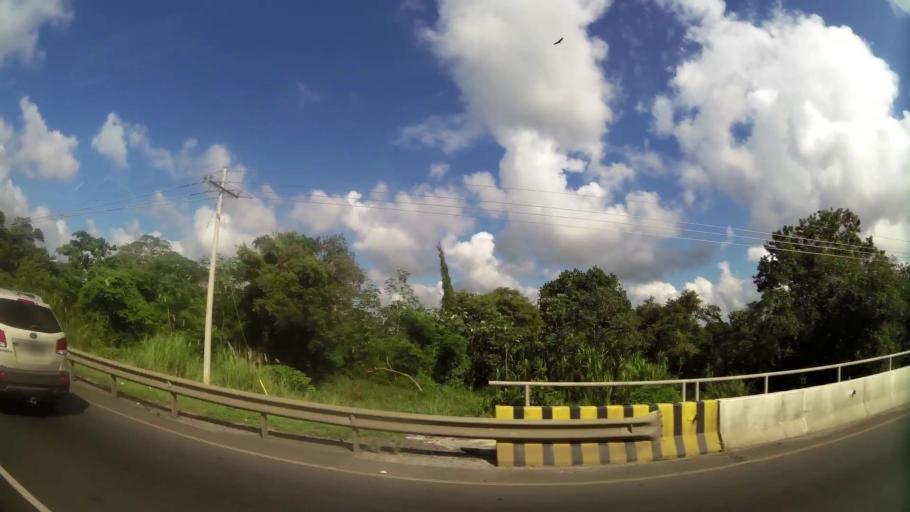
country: PA
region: Panama
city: Nuevo Arraijan
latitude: 8.9126
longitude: -79.7225
